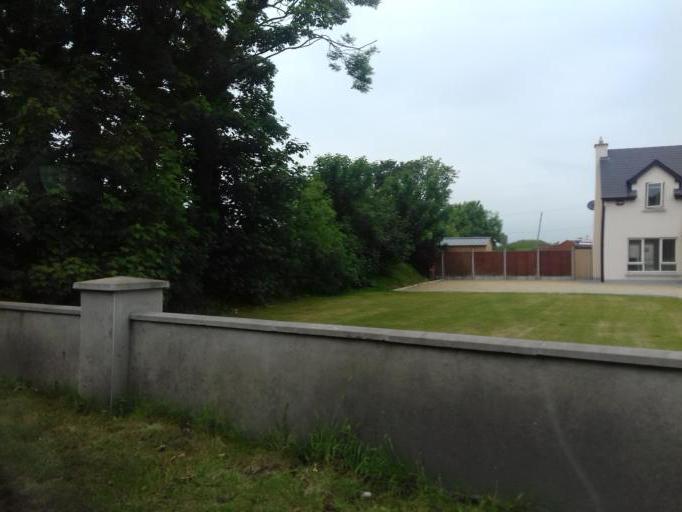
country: IE
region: Leinster
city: Donabate
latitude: 53.4702
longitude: -6.1288
